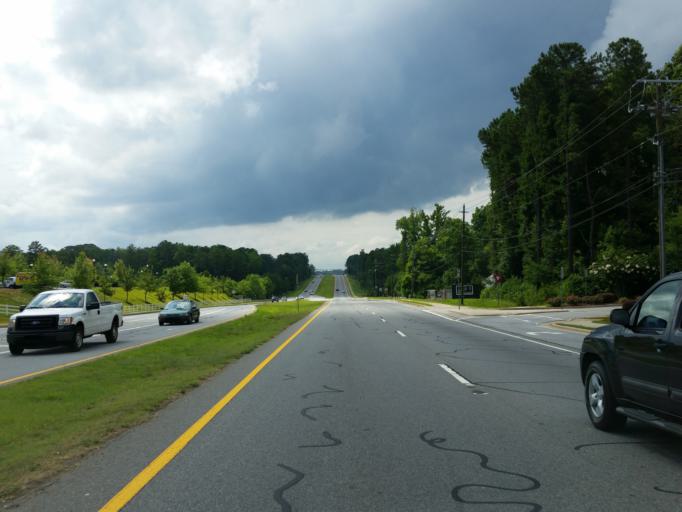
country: US
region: Georgia
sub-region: Cherokee County
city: Woodstock
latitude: 34.0813
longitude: -84.4529
